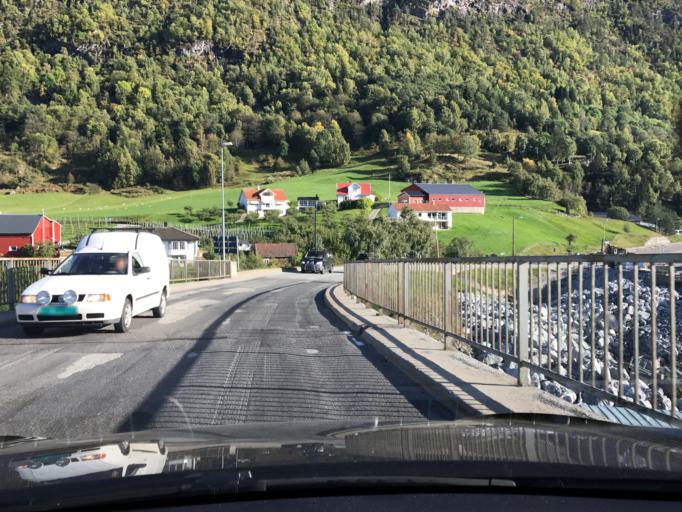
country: NO
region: Sogn og Fjordane
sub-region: Sogndal
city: Sogndalsfjora
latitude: 61.2311
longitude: 7.1219
